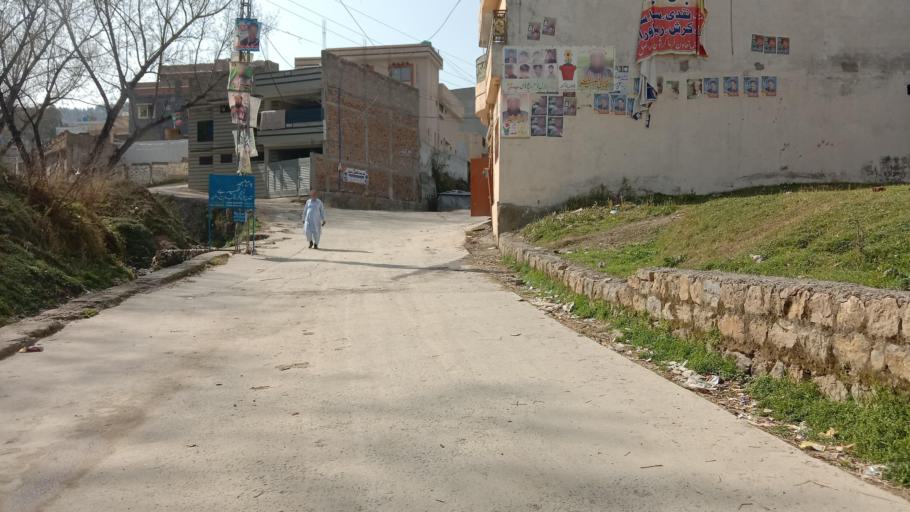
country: PK
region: Khyber Pakhtunkhwa
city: Abbottabad
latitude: 34.1759
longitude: 73.2158
